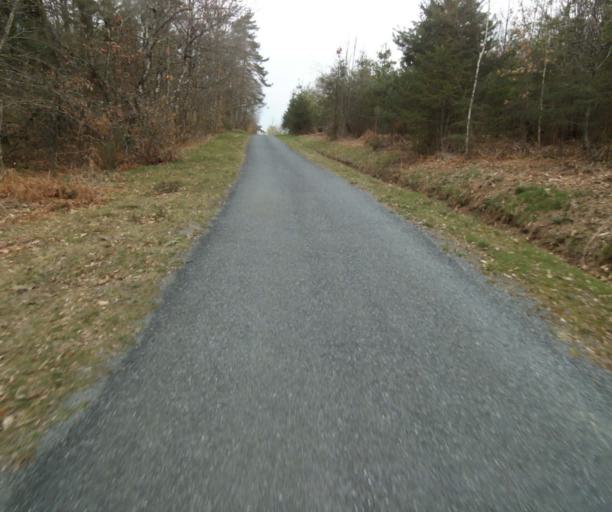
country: FR
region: Limousin
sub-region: Departement de la Correze
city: Correze
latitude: 45.2928
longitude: 1.9250
